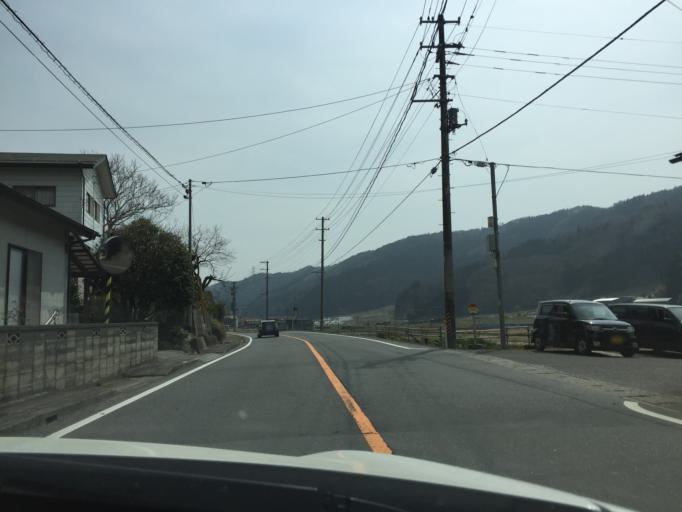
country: JP
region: Fukushima
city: Ishikawa
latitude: 37.1175
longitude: 140.5045
